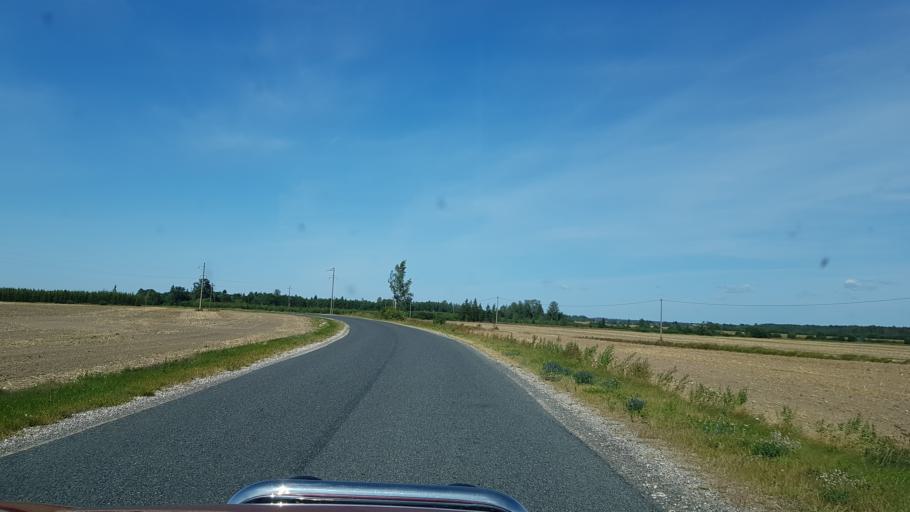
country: EE
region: Laeaene-Virumaa
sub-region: Rakke vald
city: Rakke
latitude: 59.0211
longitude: 26.3530
